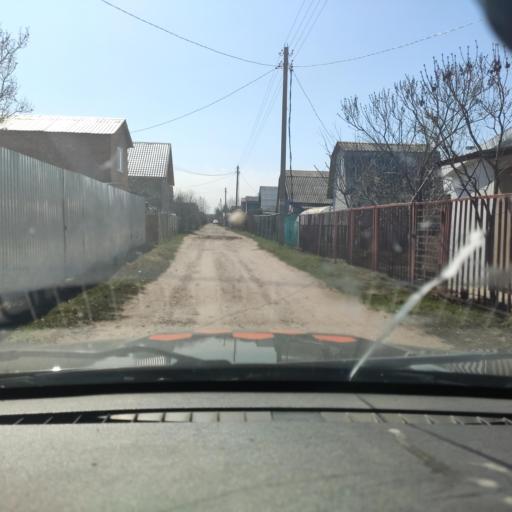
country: RU
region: Samara
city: Tol'yatti
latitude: 53.5849
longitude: 49.3147
